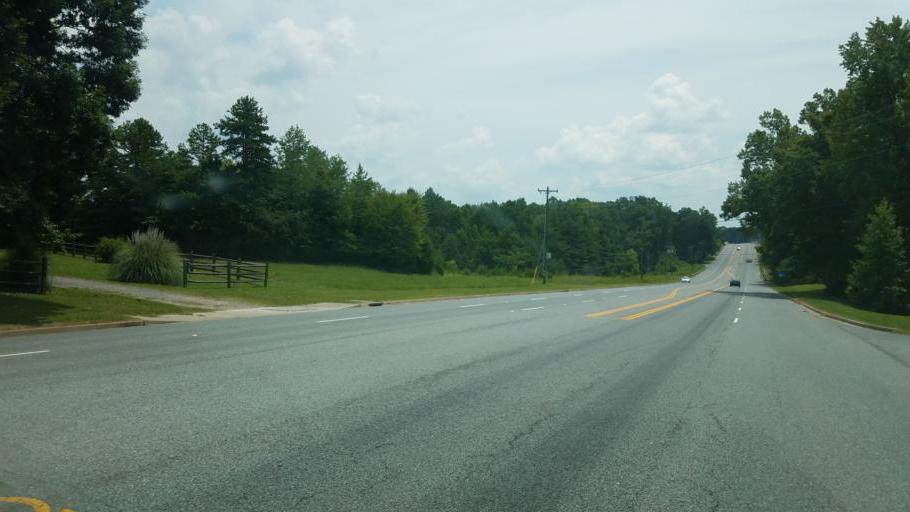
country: US
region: South Carolina
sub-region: York County
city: York
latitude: 35.0197
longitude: -81.2754
